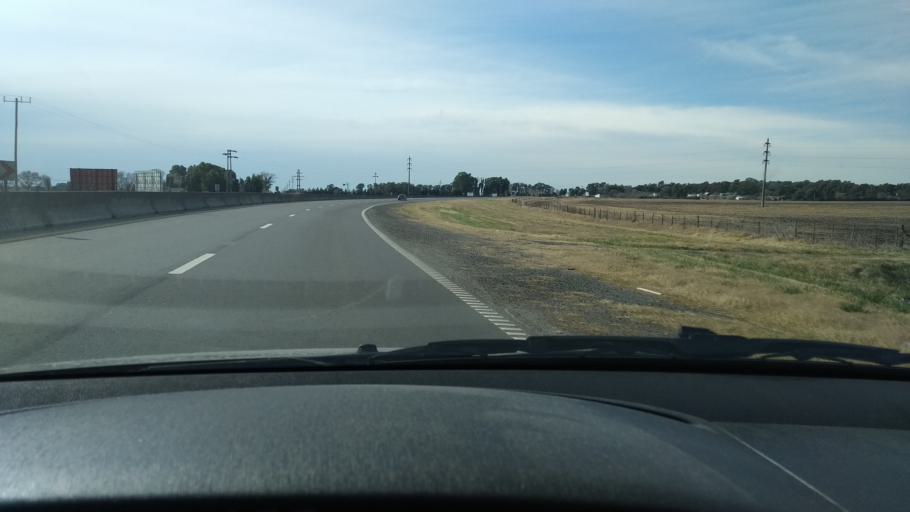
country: AR
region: Buenos Aires
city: Olavarria
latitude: -36.9043
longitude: -60.1891
